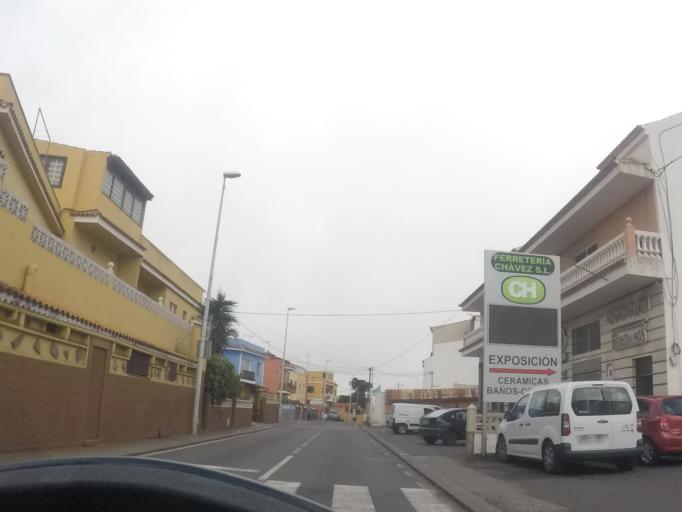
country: ES
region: Canary Islands
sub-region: Provincia de Santa Cruz de Tenerife
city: Tacoronte
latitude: 28.4960
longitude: -16.3777
